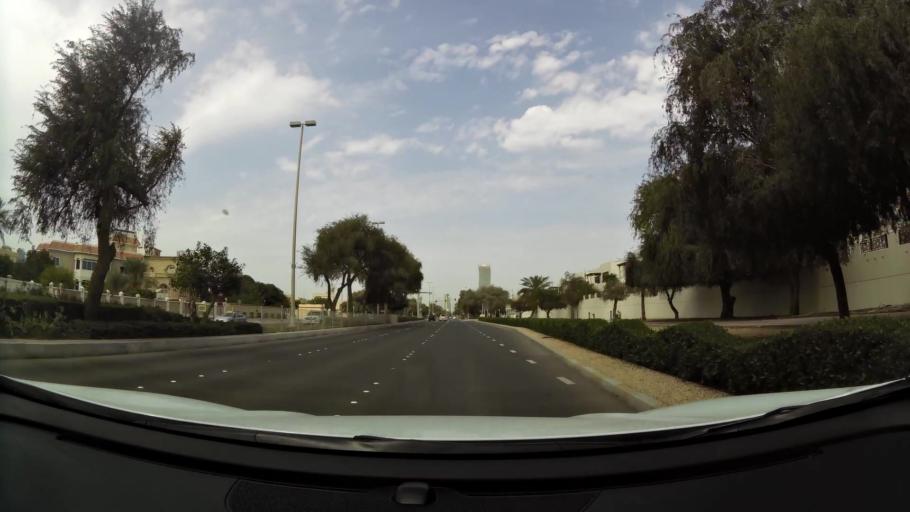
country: AE
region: Abu Dhabi
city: Abu Dhabi
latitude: 24.4566
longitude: 54.3498
